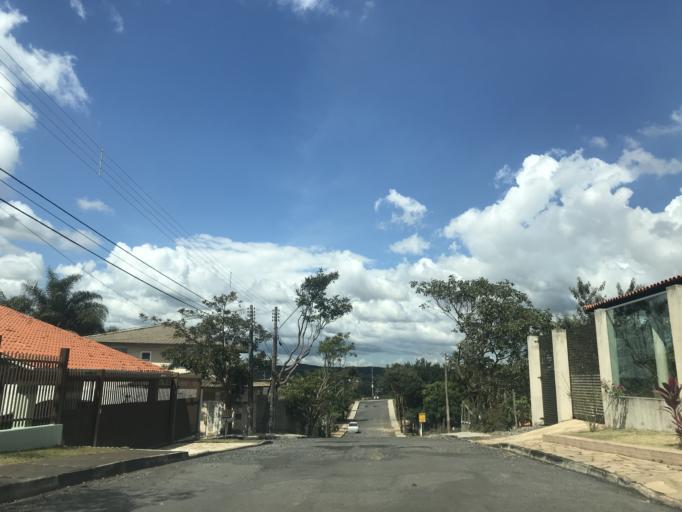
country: BR
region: Federal District
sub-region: Brasilia
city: Brasilia
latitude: -15.8657
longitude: -47.7540
